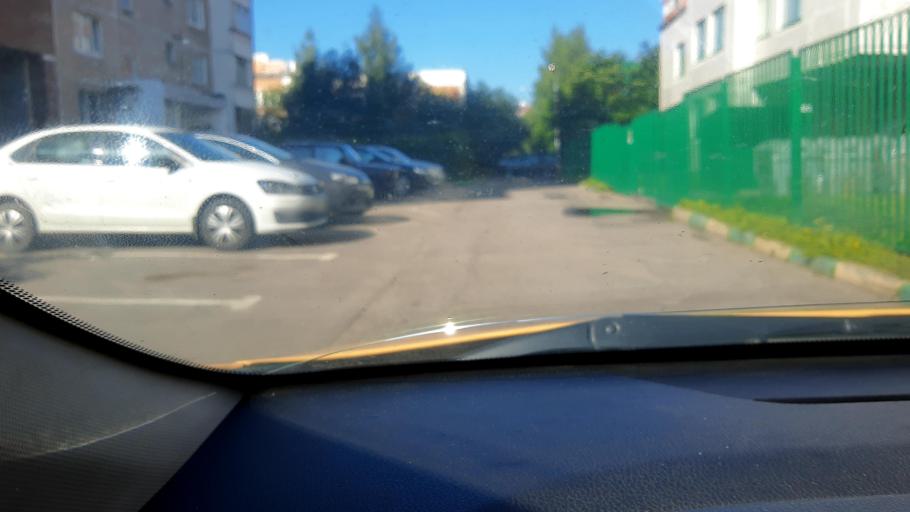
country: RU
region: Moskovskaya
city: Kommunarka
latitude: 55.5345
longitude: 37.5244
